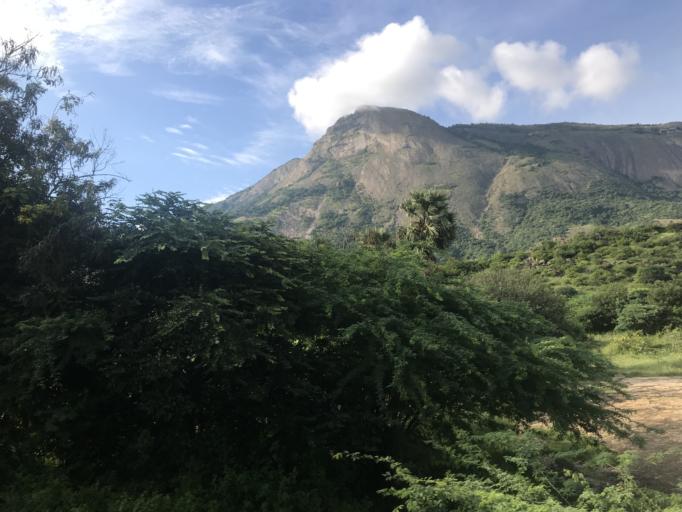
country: IN
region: Tamil Nadu
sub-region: Coimbatore
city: Madukkarai
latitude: 10.8959
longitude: 76.8866
